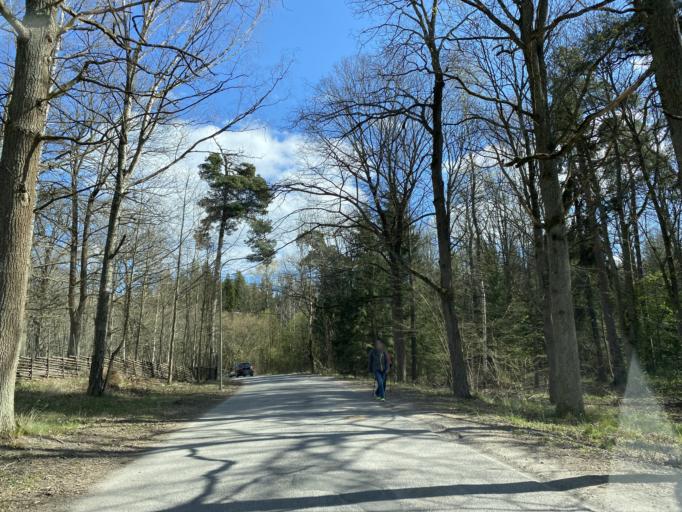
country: SE
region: Stockholm
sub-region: Nacka Kommun
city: Nacka
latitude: 59.3307
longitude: 18.1411
